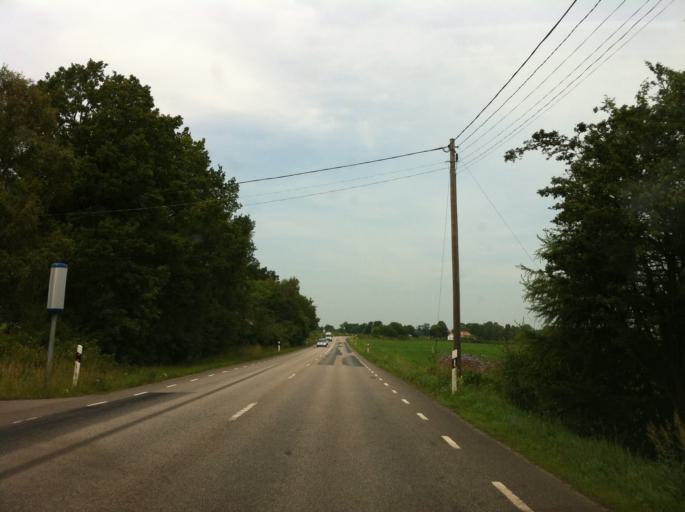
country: SE
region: Kalmar
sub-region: Torsas Kommun
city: Torsas
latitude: 56.4140
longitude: 16.0690
